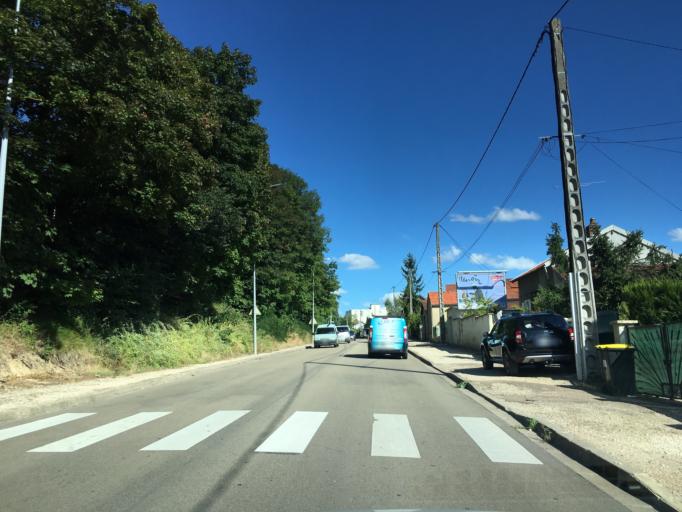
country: FR
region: Bourgogne
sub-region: Departement de l'Yonne
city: Auxerre
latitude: 47.7892
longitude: 3.5513
